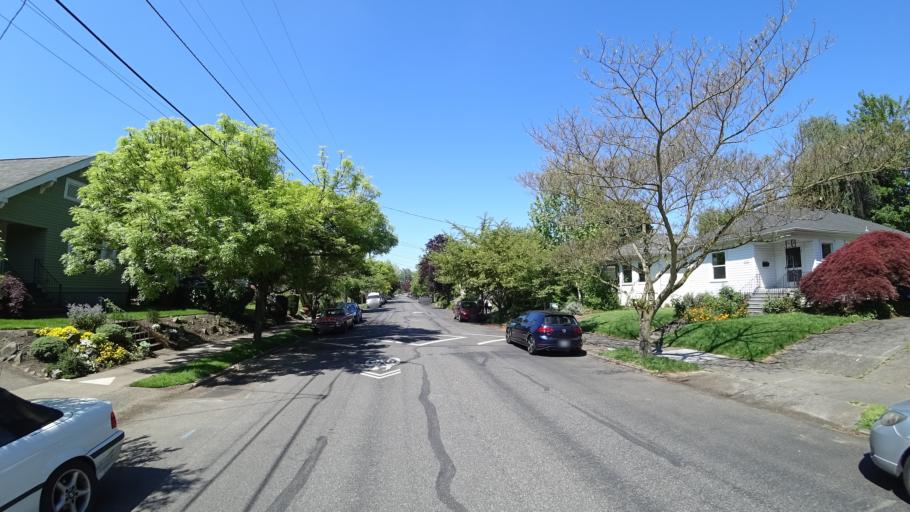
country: US
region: Oregon
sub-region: Multnomah County
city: Portland
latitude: 45.5080
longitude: -122.6284
